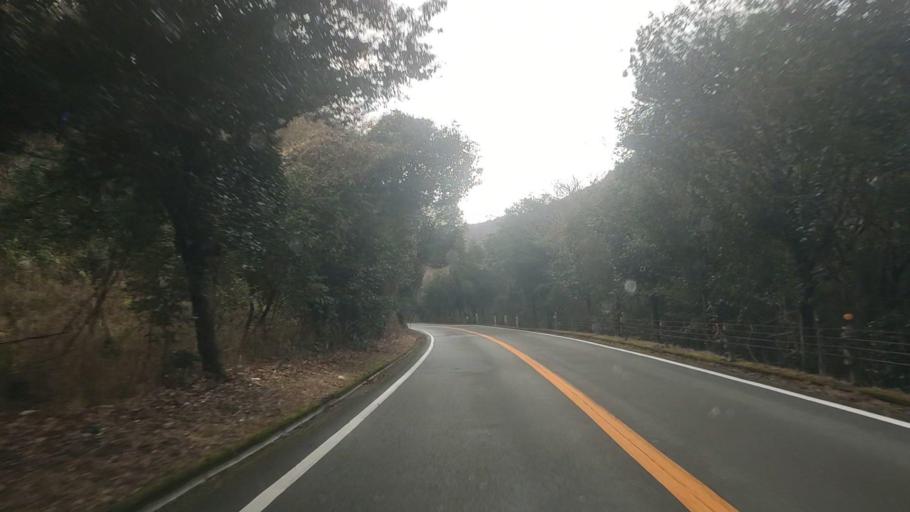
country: JP
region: Kumamoto
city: Hitoyoshi
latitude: 32.1263
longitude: 130.8135
